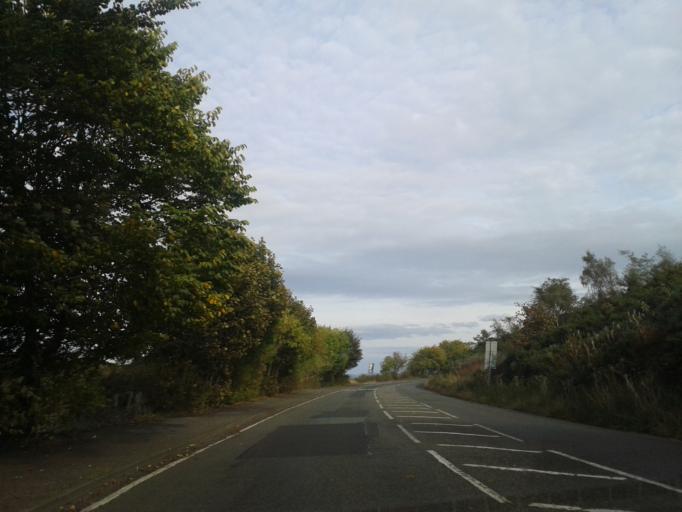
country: GB
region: Scotland
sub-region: Edinburgh
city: Edinburgh
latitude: 55.9180
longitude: -3.2020
